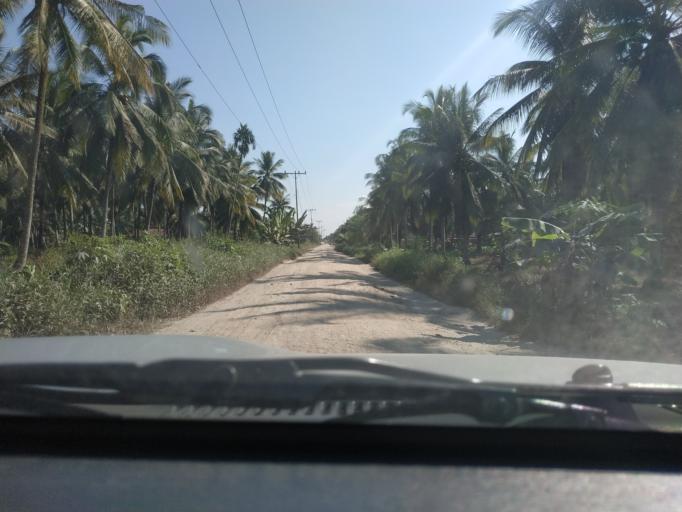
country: ID
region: North Sumatra
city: Tanjungbalai
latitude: 2.8309
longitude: 99.9699
